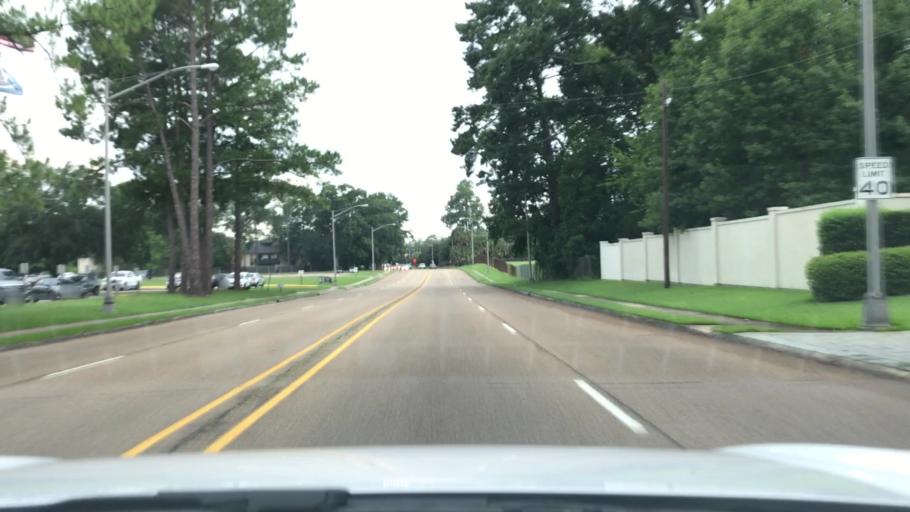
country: US
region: Louisiana
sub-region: East Baton Rouge Parish
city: Baton Rouge
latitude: 30.4390
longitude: -91.1336
